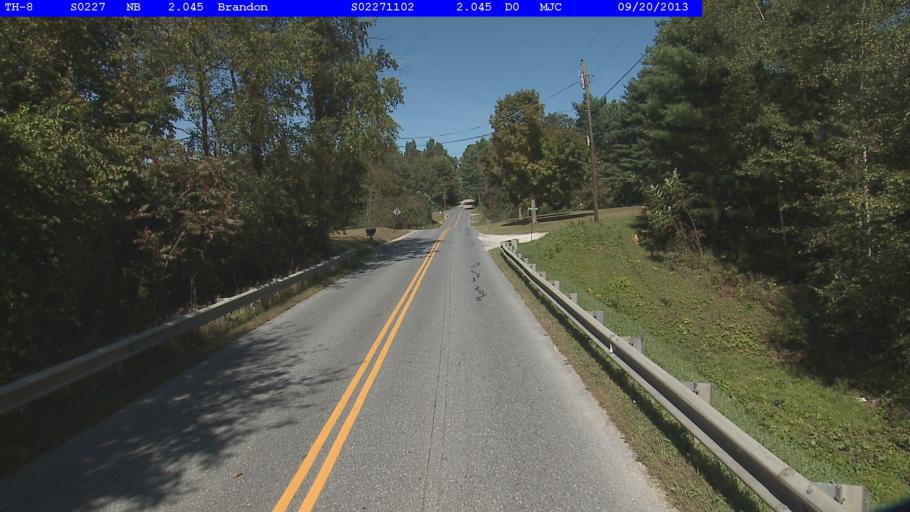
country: US
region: Vermont
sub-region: Rutland County
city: Brandon
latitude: 43.8038
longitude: -73.0560
